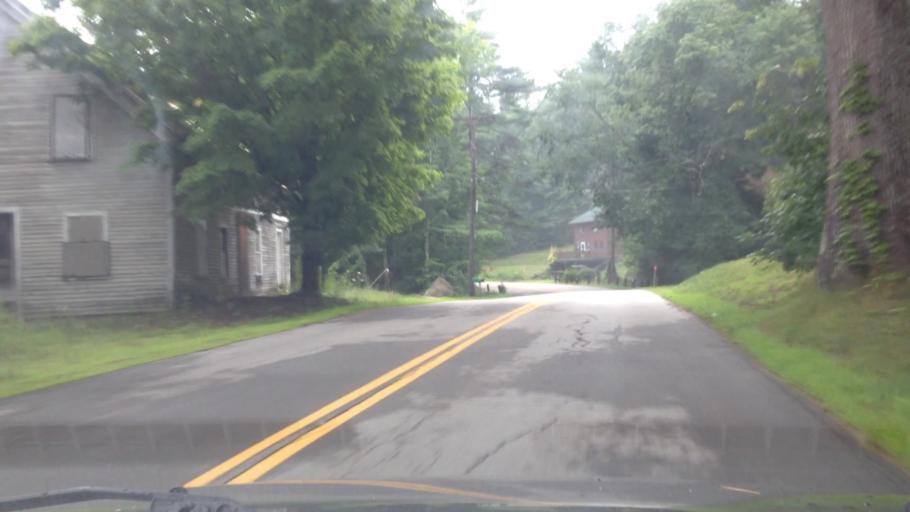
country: US
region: New Hampshire
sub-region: Cheshire County
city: Swanzey
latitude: 42.8484
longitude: -72.2623
